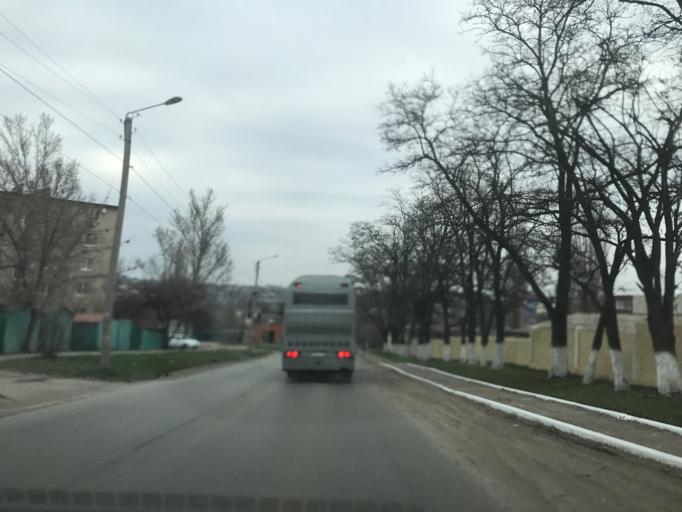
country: RU
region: Rostov
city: Novocherkassk
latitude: 47.4023
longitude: 40.0761
